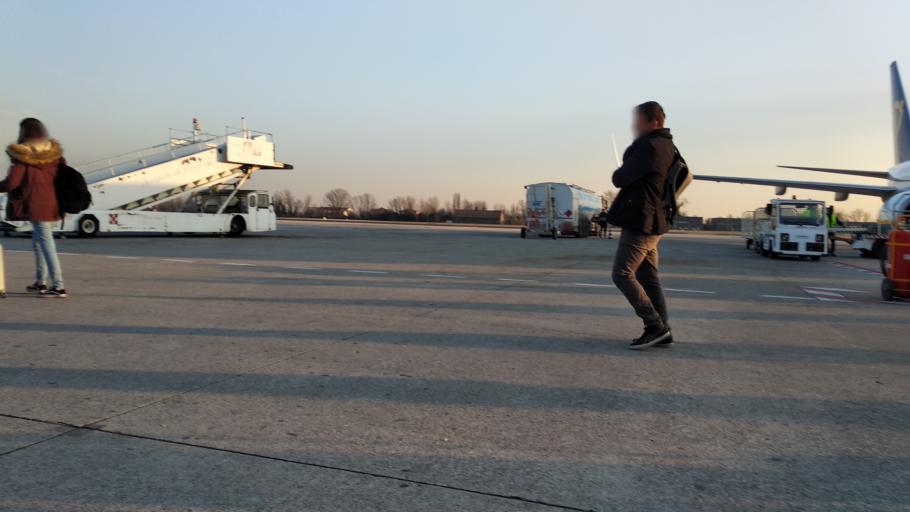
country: IT
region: Veneto
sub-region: Provincia di Treviso
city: Treviso
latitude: 45.6540
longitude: 12.2037
